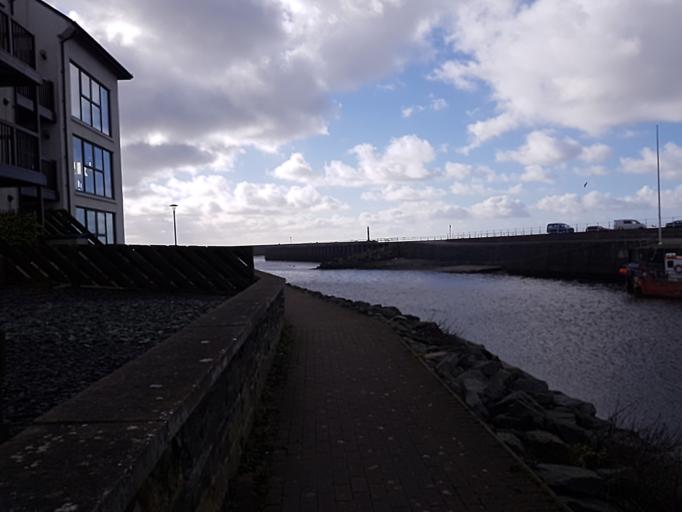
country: GB
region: Wales
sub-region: County of Ceredigion
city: Aberystwyth
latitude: 52.4088
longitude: -4.0879
